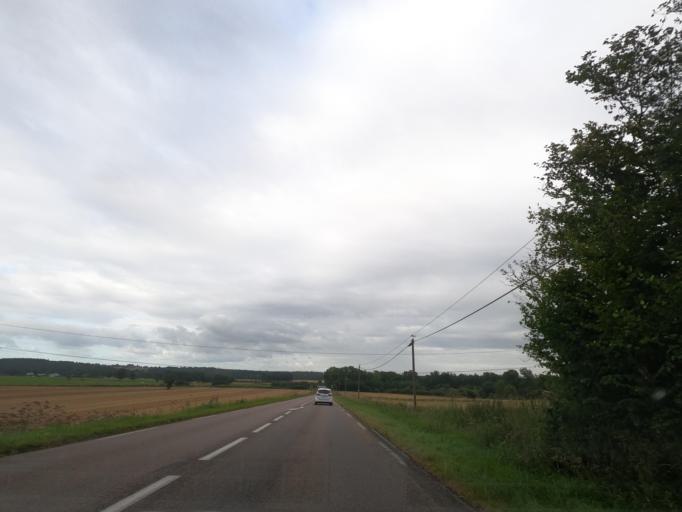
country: FR
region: Haute-Normandie
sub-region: Departement de l'Eure
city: Bourgtheroulde-Infreville
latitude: 49.2676
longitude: 0.8115
